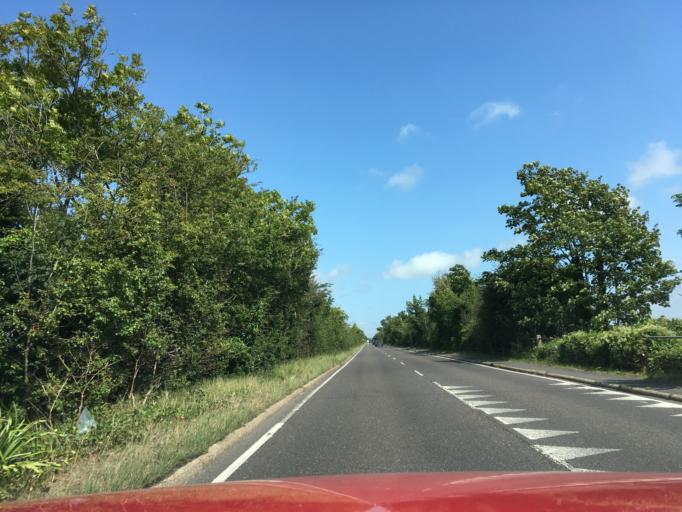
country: GB
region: England
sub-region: East Sussex
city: Rye
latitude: 50.9266
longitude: 0.7156
